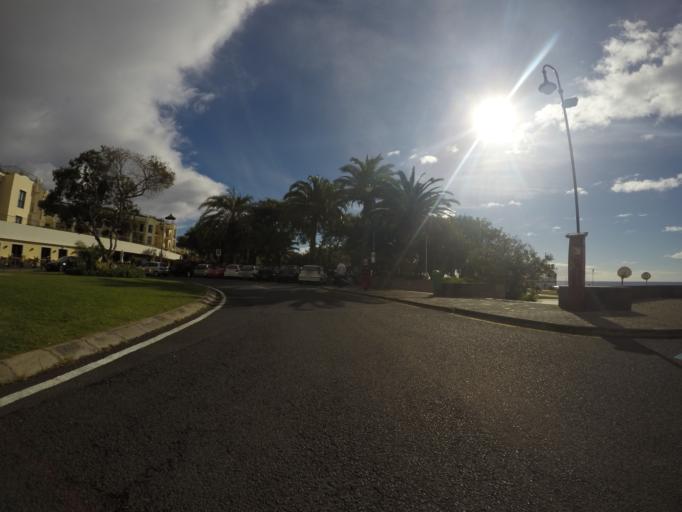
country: PT
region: Madeira
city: Camara de Lobos
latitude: 32.6366
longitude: -16.9342
